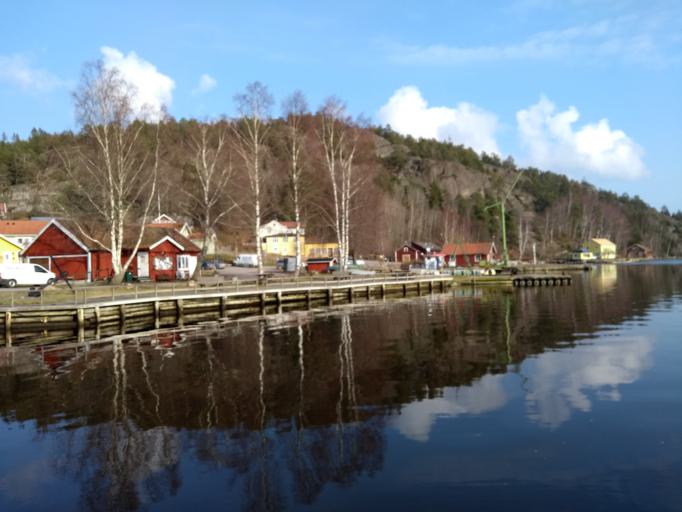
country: SE
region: Soedermanland
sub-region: Nykopings Kommun
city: Olstorp
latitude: 58.6380
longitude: 16.6311
